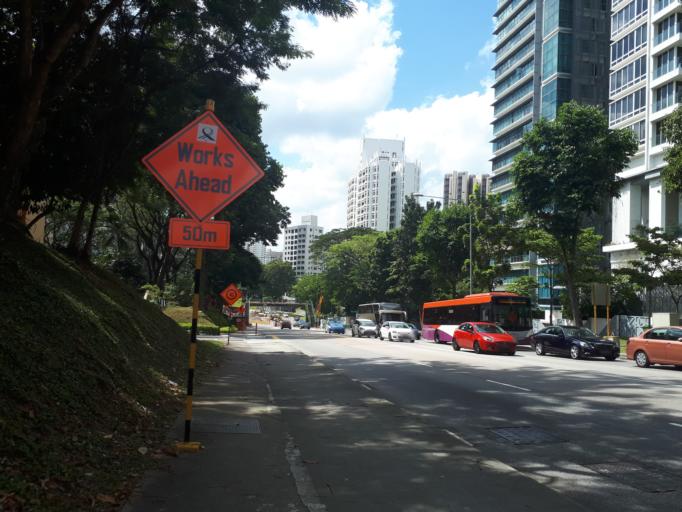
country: SG
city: Singapore
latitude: 1.2960
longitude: 103.8352
